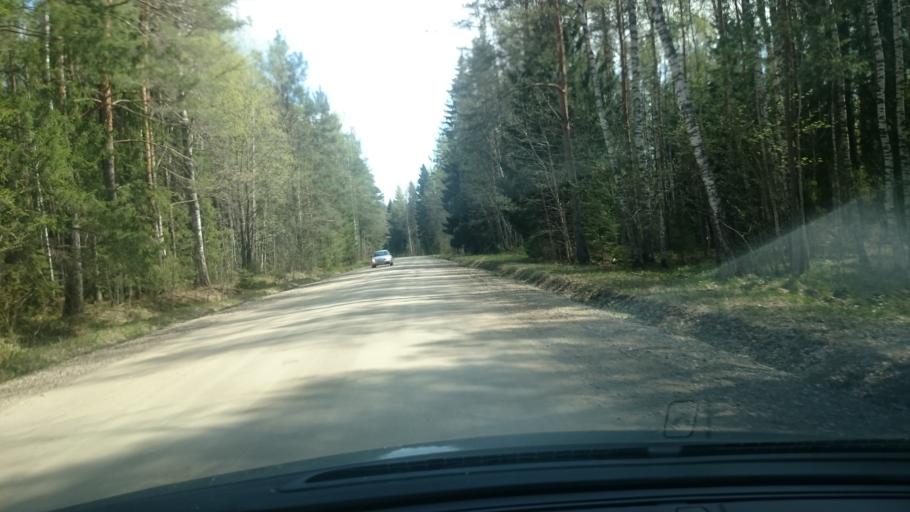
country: EE
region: Ida-Virumaa
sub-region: Sillamaee linn
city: Sillamae
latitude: 59.0771
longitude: 27.7012
